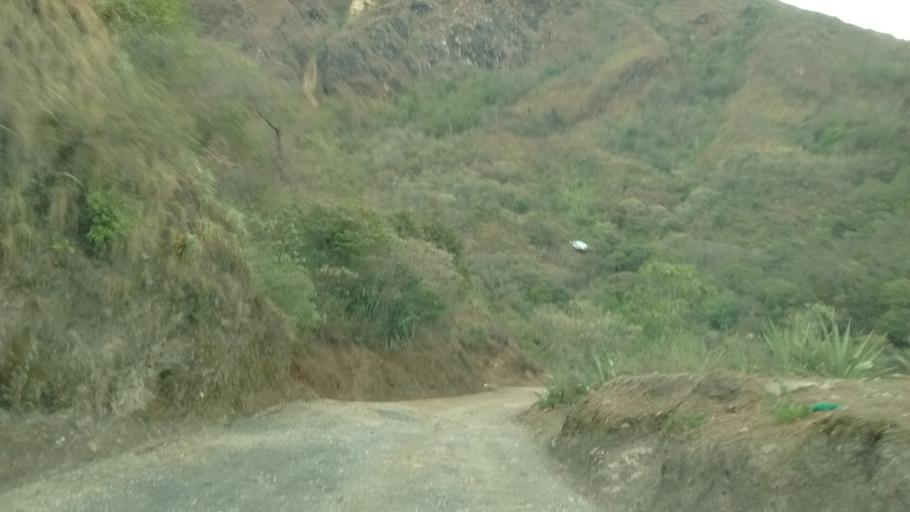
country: CO
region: Cauca
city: Almaguer
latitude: 1.8424
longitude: -76.9098
